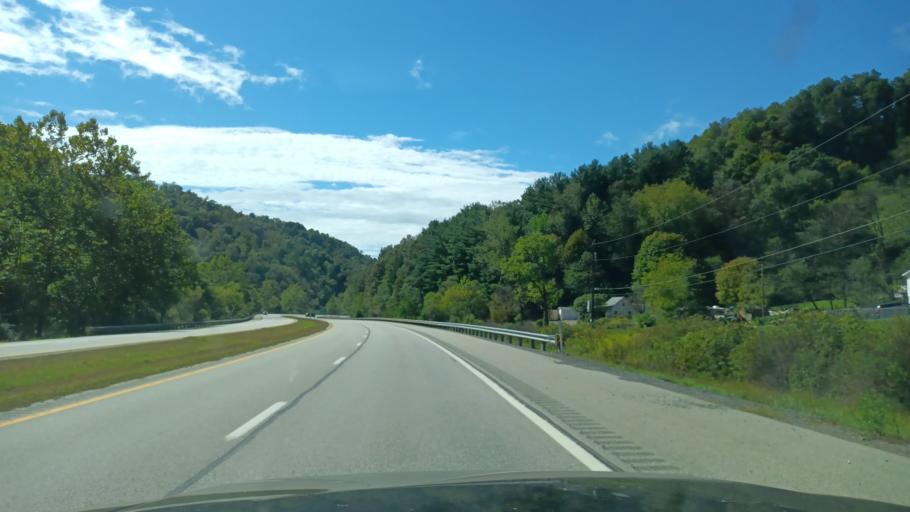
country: US
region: West Virginia
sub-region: Harrison County
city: Salem
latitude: 39.2924
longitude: -80.6344
